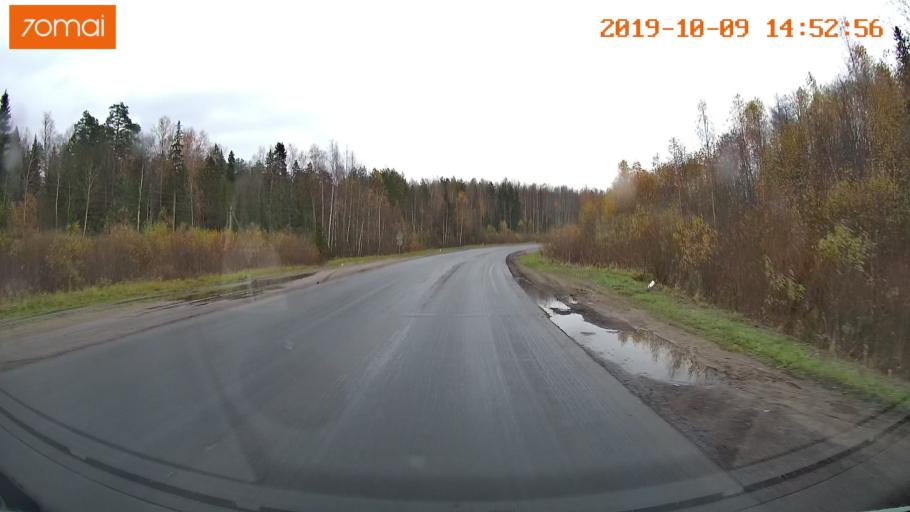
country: RU
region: Kostroma
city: Chistyye Bory
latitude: 58.3736
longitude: 41.6345
